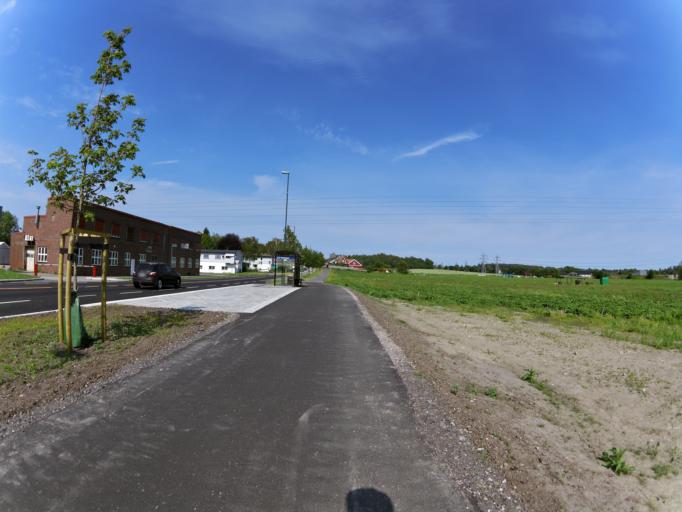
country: NO
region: Ostfold
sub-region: Sarpsborg
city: Sarpsborg
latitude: 59.2657
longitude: 11.1217
